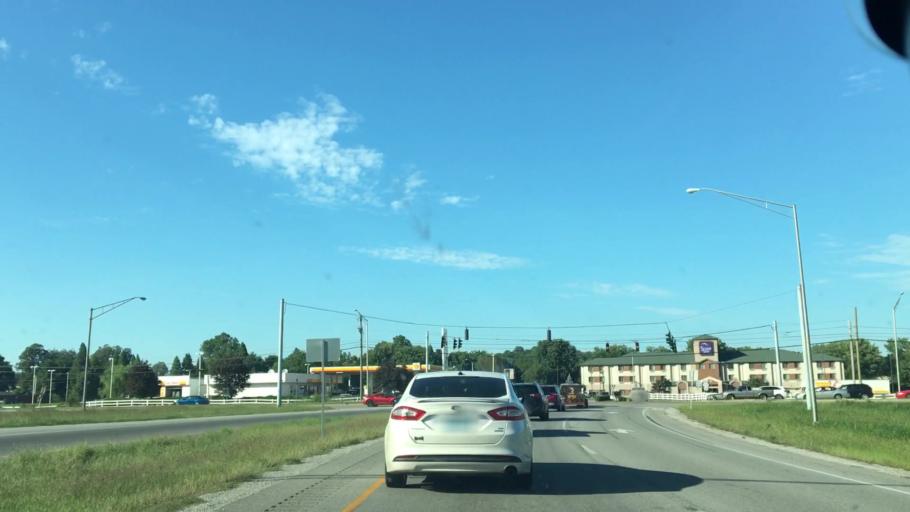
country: US
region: Kentucky
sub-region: Daviess County
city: Owensboro
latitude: 37.7743
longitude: -87.1659
